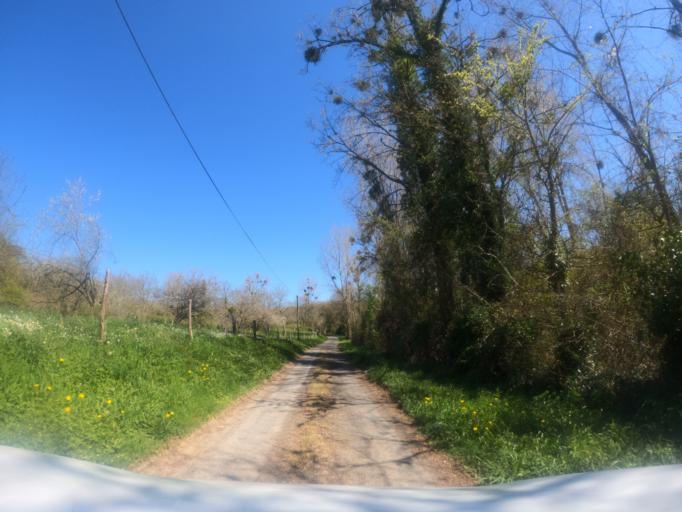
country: FR
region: Pays de la Loire
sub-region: Departement de la Vendee
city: Fontenay-le-Comte
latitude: 46.4455
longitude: -0.8650
